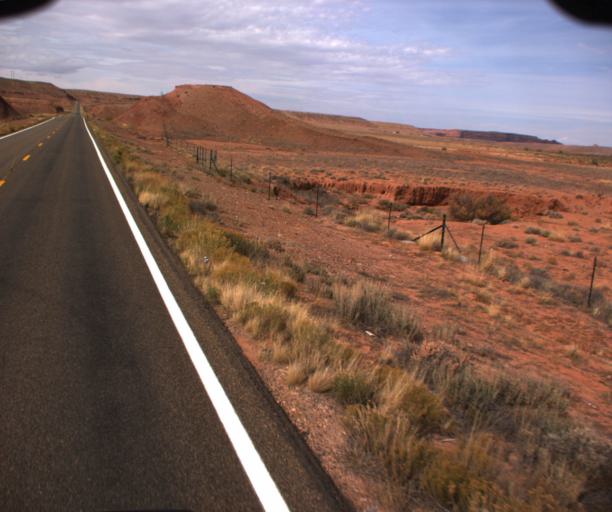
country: US
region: Arizona
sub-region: Apache County
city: Many Farms
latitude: 36.5366
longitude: -109.5164
